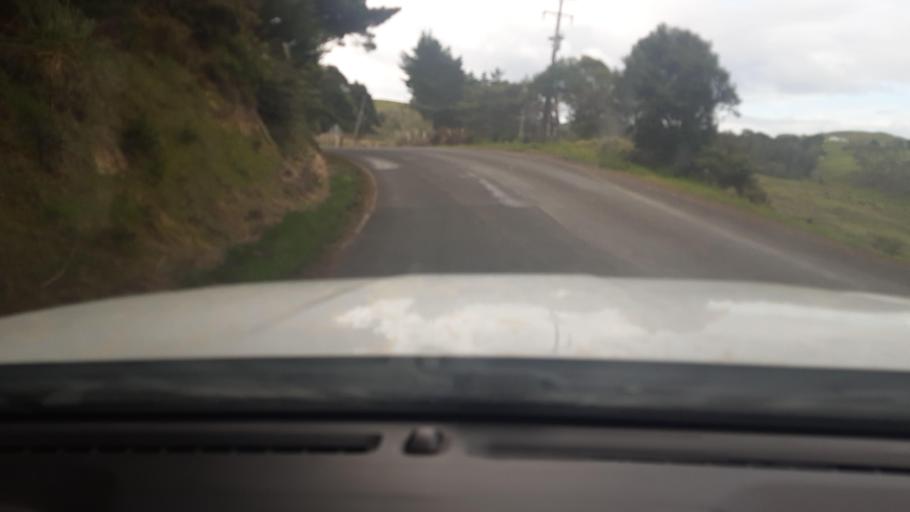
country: NZ
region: Northland
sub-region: Far North District
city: Ahipara
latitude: -35.2723
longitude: 173.2091
